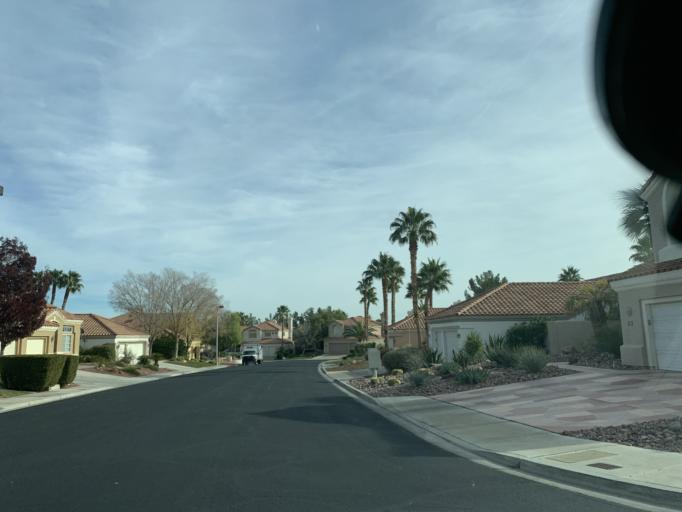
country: US
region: Nevada
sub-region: Clark County
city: Summerlin South
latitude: 36.1530
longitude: -115.3013
